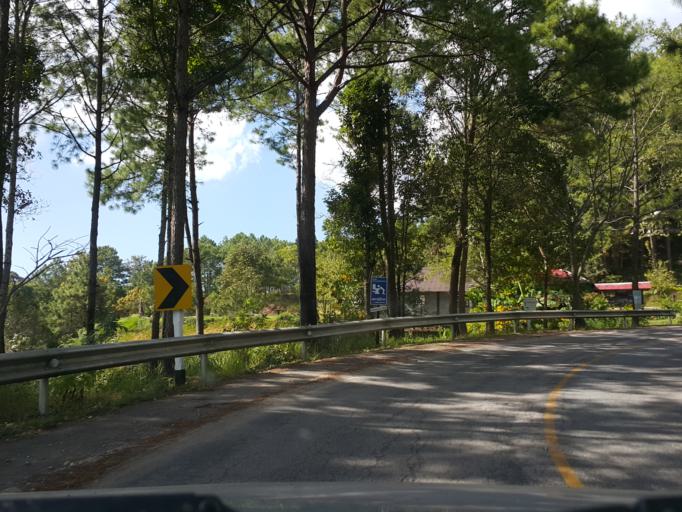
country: TH
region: Mae Hong Son
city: Mae Hi
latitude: 19.2508
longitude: 98.6390
